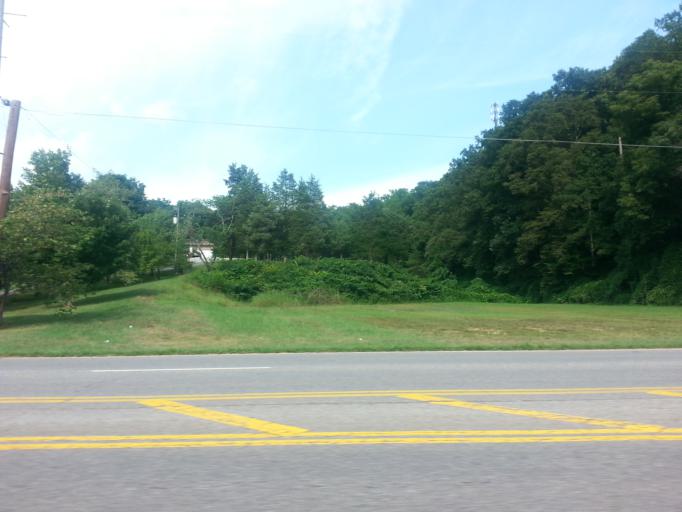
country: US
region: Tennessee
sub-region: Knox County
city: Knoxville
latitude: 35.9129
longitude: -83.8553
